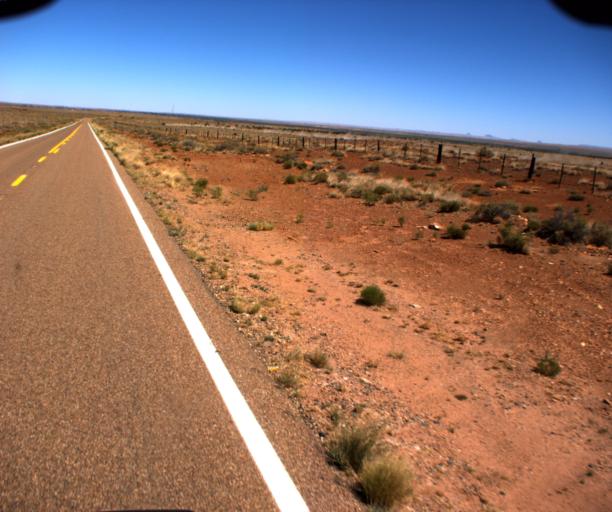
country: US
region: Arizona
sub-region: Navajo County
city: Winslow
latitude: 34.9357
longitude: -110.6410
